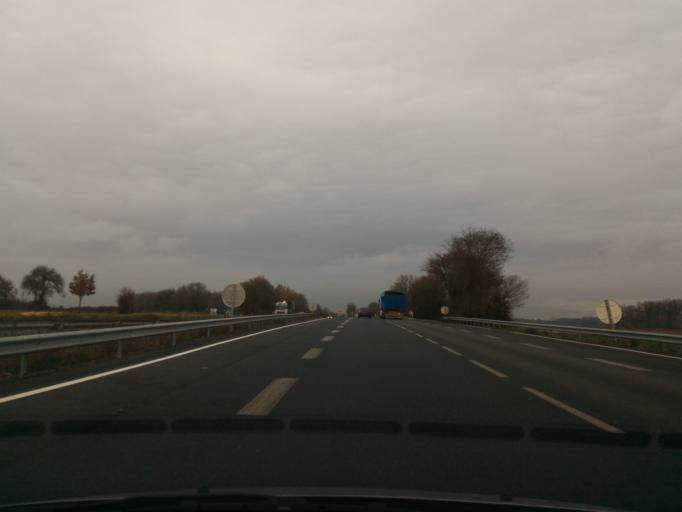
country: FR
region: Poitou-Charentes
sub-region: Departement de la Vienne
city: Iteuil
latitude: 46.4823
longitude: 0.2719
